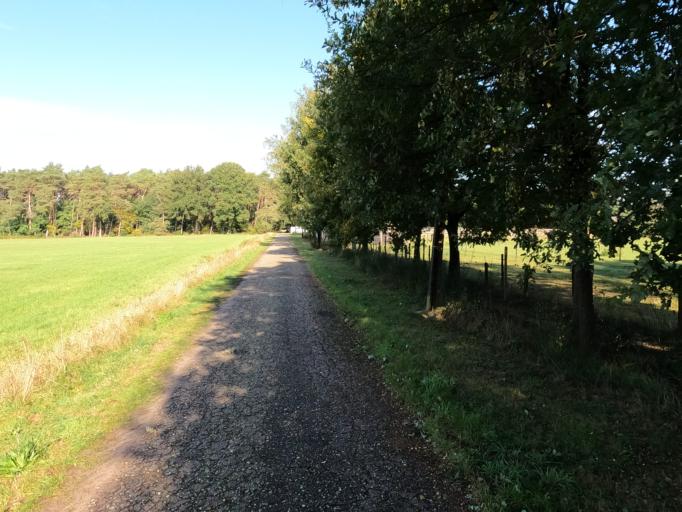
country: BE
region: Flanders
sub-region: Provincie Antwerpen
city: Zandhoven
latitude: 51.2330
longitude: 4.6710
